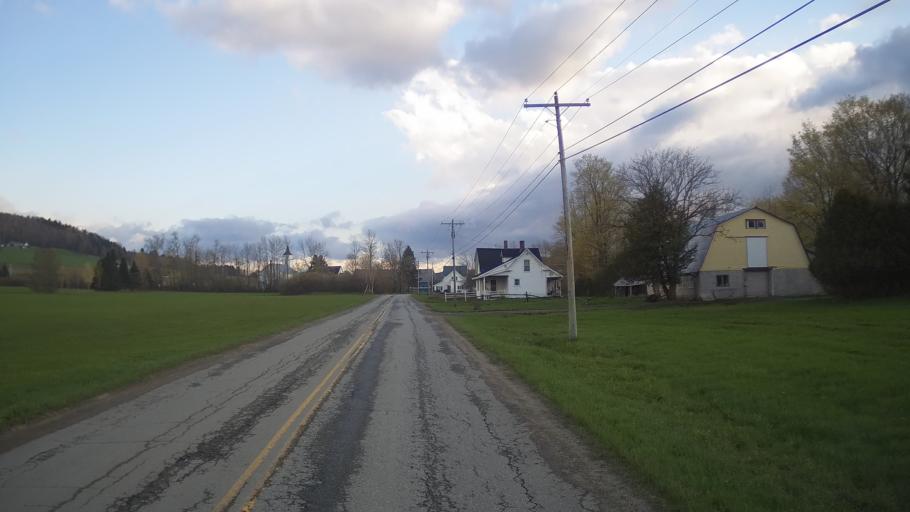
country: US
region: Vermont
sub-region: Orleans County
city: Newport
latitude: 44.7312
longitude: -72.2234
